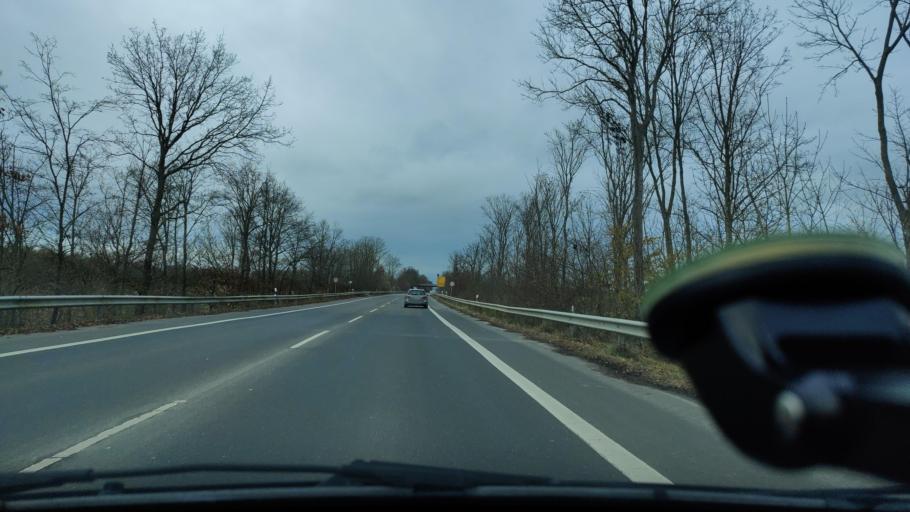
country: DE
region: North Rhine-Westphalia
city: Julich
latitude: 50.9769
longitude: 6.3496
